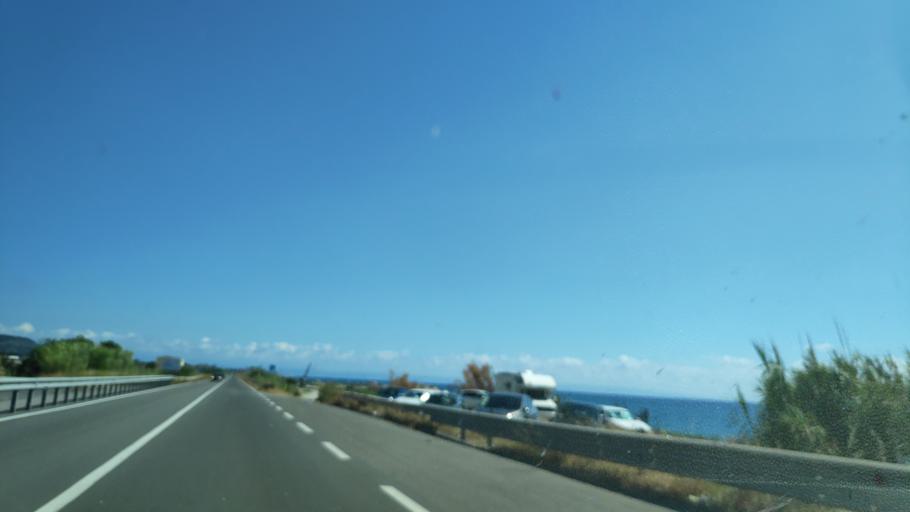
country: IT
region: Calabria
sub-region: Provincia di Cosenza
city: Campora San Giovanni
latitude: 39.0628
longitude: 16.0916
